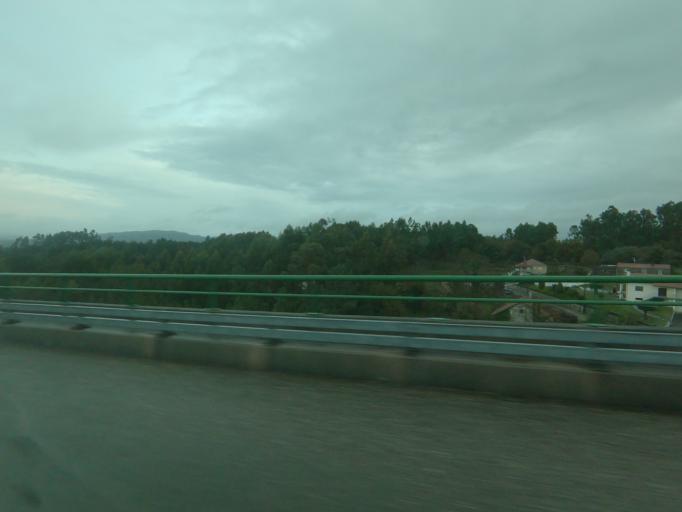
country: PT
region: Viana do Castelo
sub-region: Vila Nova de Cerveira
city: Vila Nova de Cerveira
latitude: 41.9544
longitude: -8.6727
